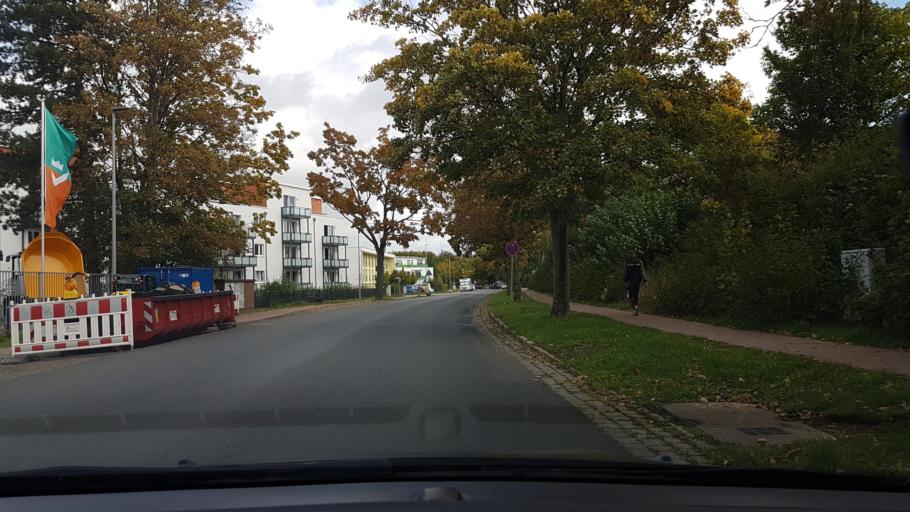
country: DE
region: Lower Saxony
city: Ronnenberg
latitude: 52.3453
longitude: 9.6759
